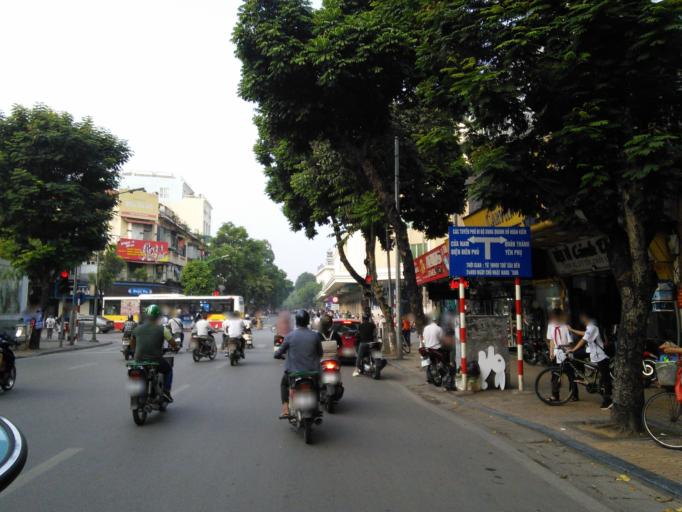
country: VN
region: Ha Noi
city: Hoan Kiem
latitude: 21.0238
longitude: 105.8529
